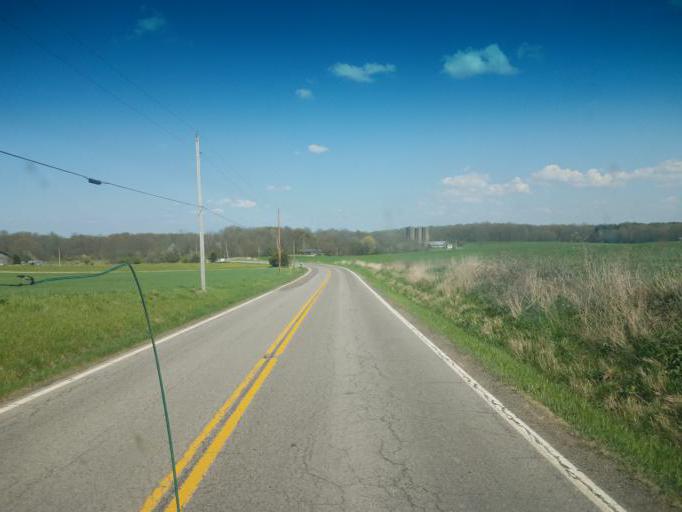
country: US
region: Ohio
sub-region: Wayne County
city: West Salem
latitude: 40.9267
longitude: -82.0463
